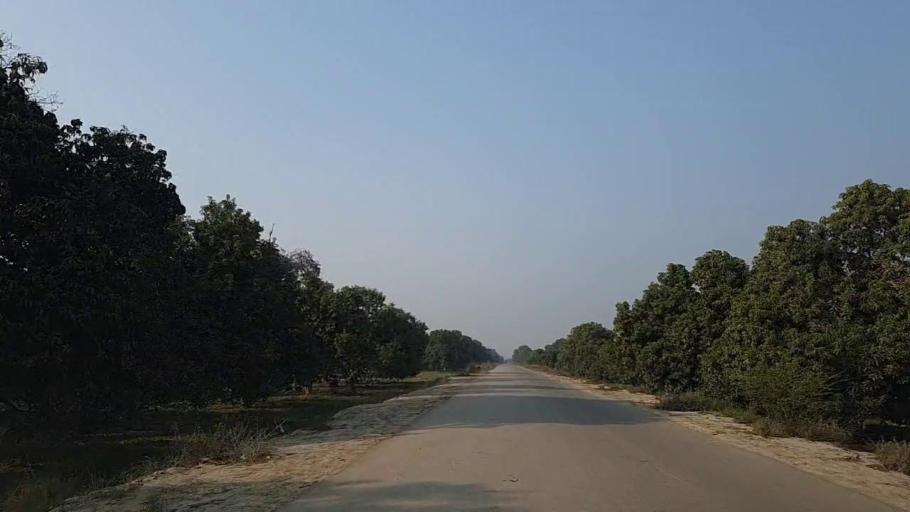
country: PK
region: Sindh
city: Sann
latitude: 26.1015
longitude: 68.1519
